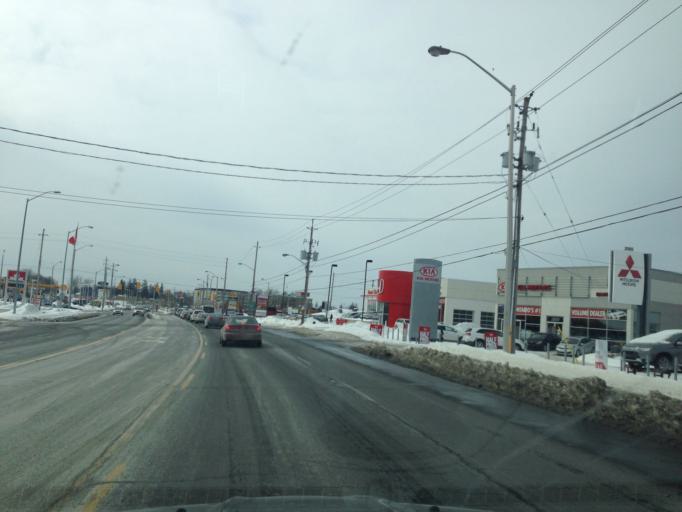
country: CA
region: Ontario
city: Ottawa
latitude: 45.3540
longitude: -75.6410
